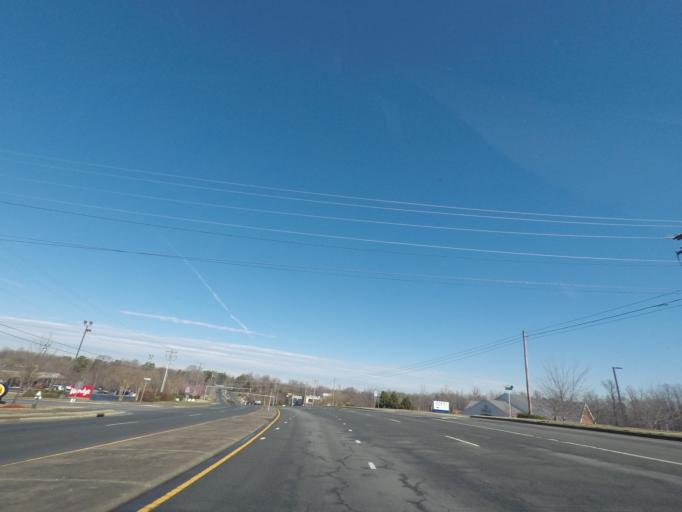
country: US
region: North Carolina
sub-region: Guilford County
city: Pleasant Garden
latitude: 36.0030
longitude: -79.7919
